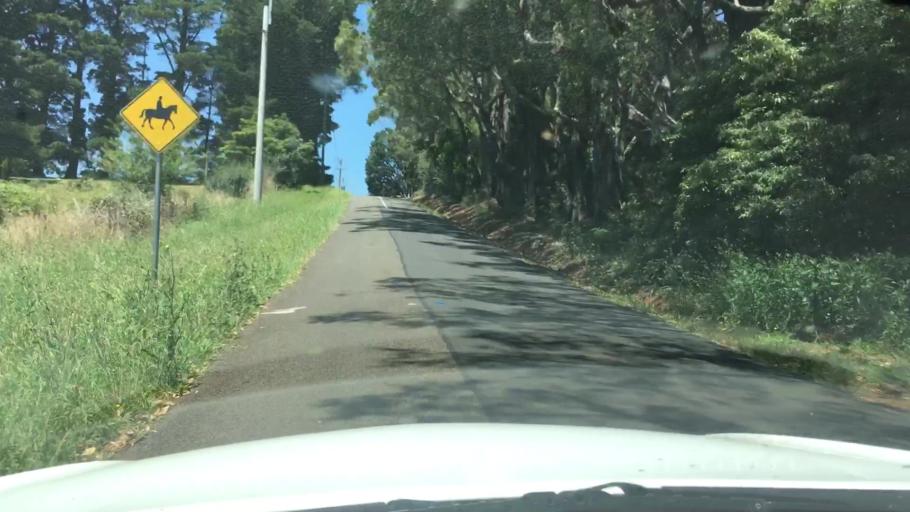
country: AU
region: Victoria
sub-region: Yarra Ranges
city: Mount Evelyn
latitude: -37.8066
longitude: 145.4232
